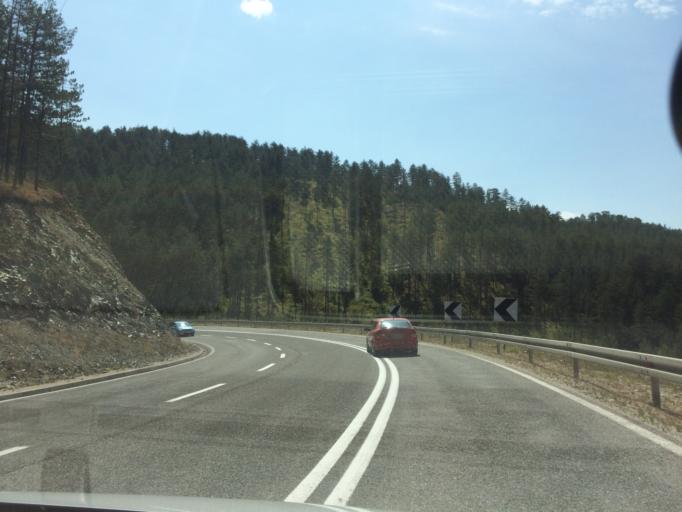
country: RS
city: Zlatibor
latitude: 43.6042
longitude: 19.7295
